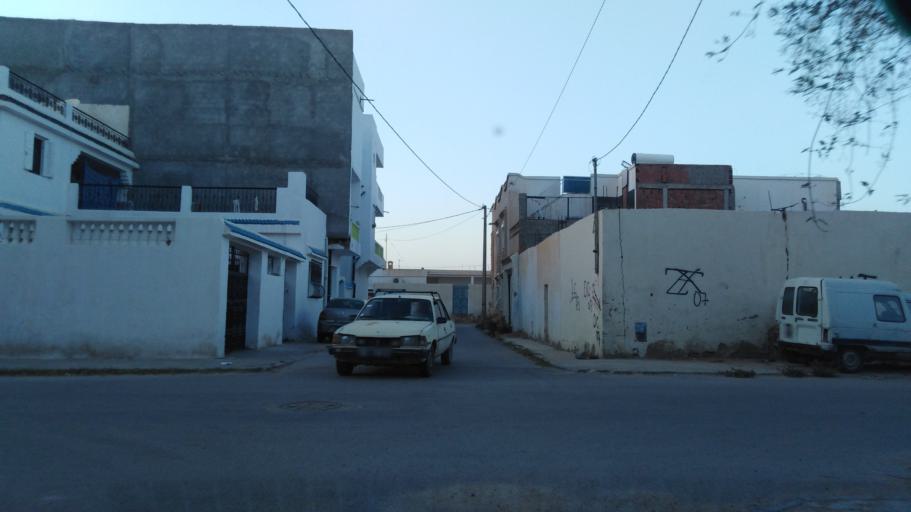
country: TN
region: Tataouine
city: Tataouine
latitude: 32.9376
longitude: 10.4524
